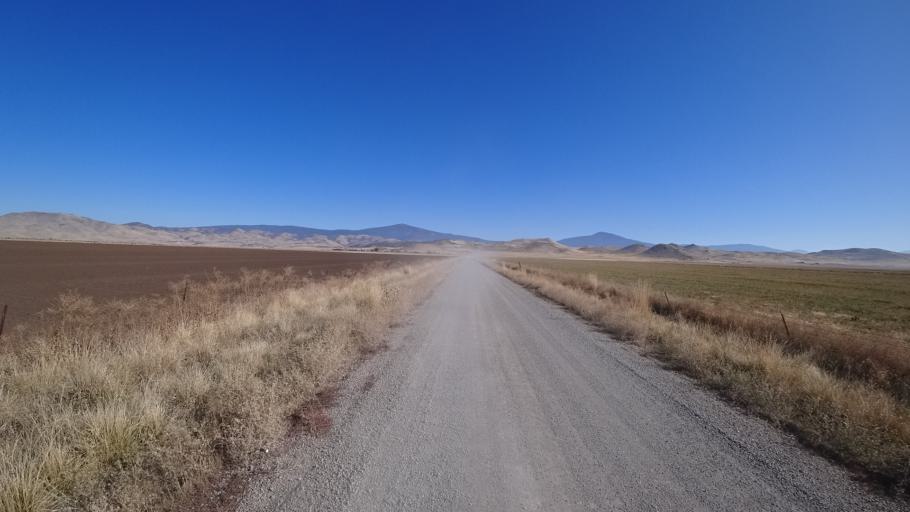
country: US
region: California
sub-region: Siskiyou County
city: Montague
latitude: 41.7865
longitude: -122.4585
